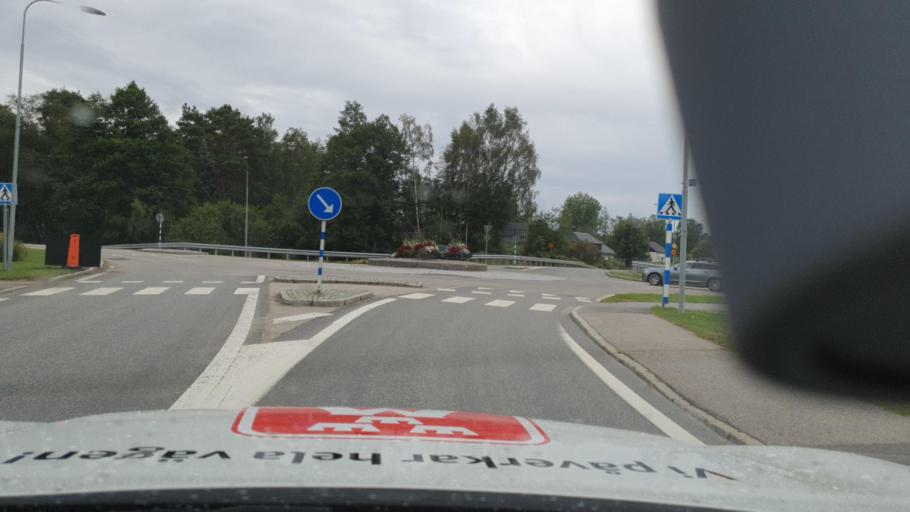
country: SE
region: Vaestra Goetaland
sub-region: Tranemo Kommun
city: Tranemo
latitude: 57.4880
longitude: 13.3414
